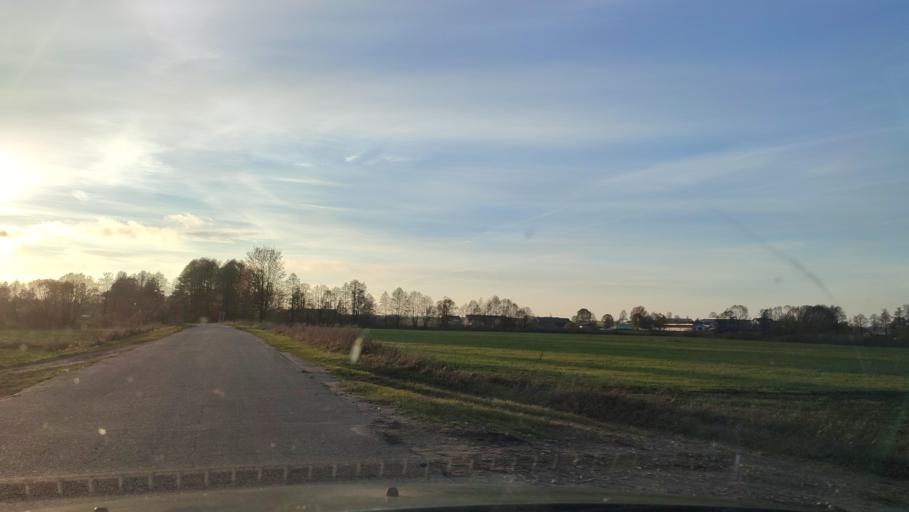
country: PL
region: Masovian Voivodeship
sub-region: Powiat mlawski
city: Dzierzgowo
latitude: 53.2601
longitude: 20.6106
